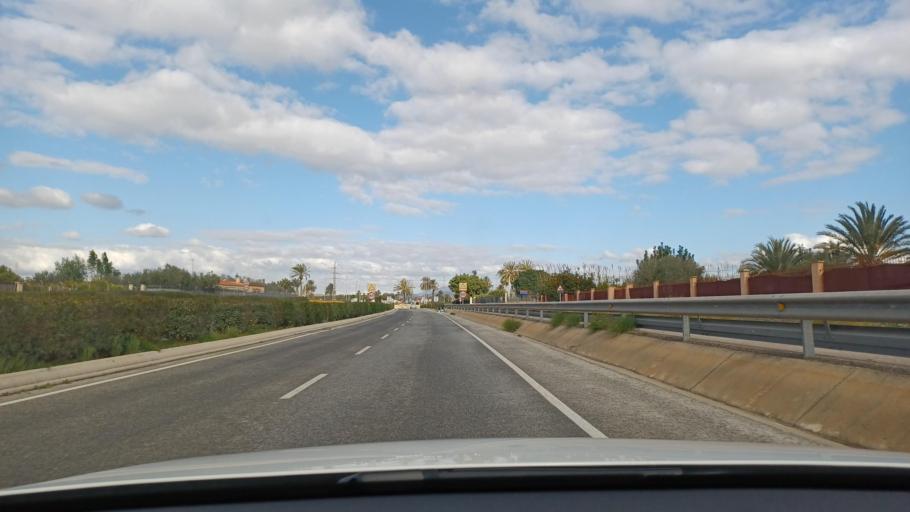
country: ES
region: Valencia
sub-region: Provincia de Alicante
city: Elche
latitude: 38.2292
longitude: -0.6994
